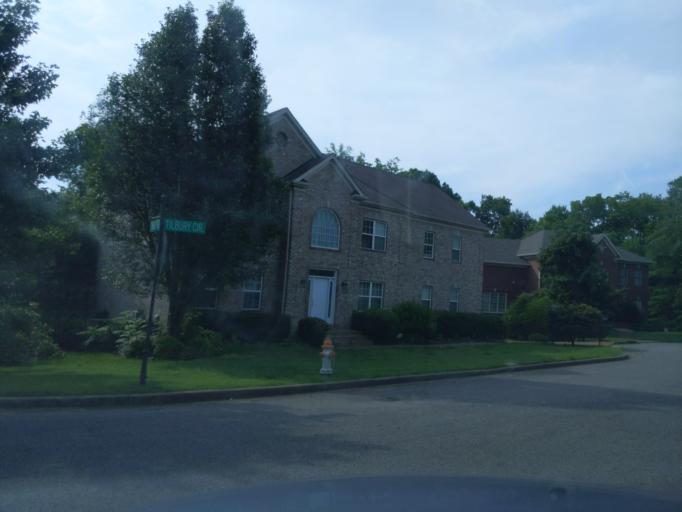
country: US
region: Tennessee
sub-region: Williamson County
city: Brentwood Estates
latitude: 36.0247
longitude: -86.7439
